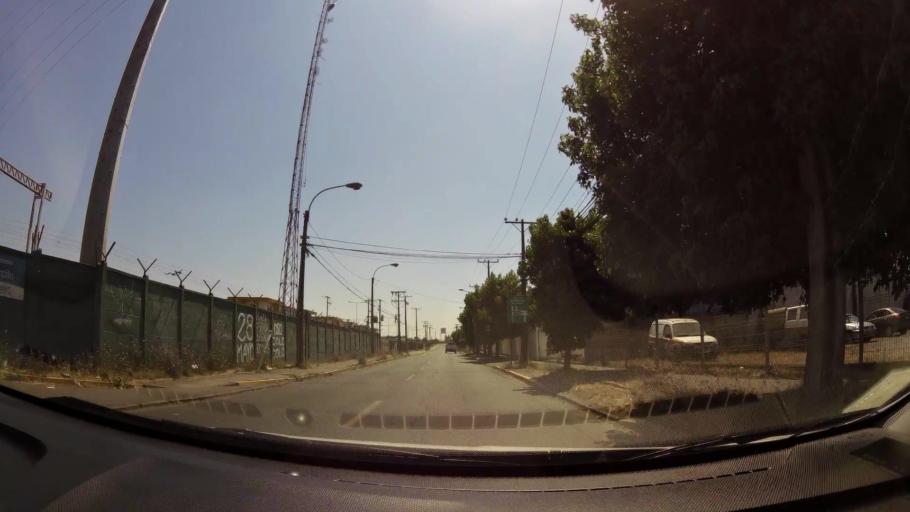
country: CL
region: Biobio
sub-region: Provincia de Concepcion
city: Concepcion
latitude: -36.8149
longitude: -73.0634
